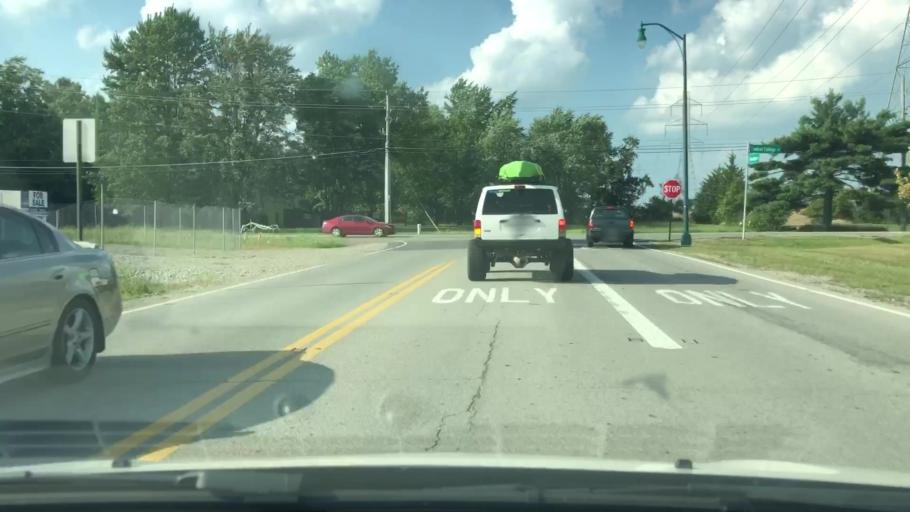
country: US
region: Ohio
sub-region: Franklin County
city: New Albany
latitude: 40.0994
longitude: -82.8485
